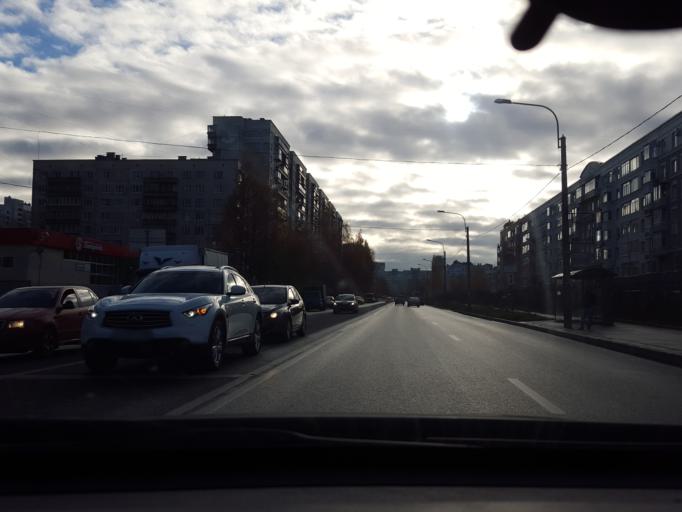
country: RU
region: St.-Petersburg
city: Ozerki
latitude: 60.0509
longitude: 30.3164
